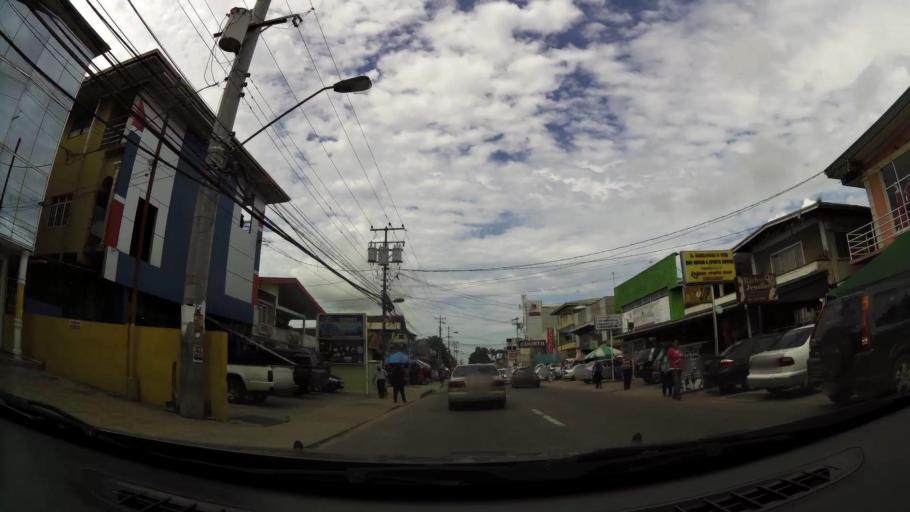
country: TT
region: Couva-Tabaquite-Talparo
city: Couva
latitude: 10.4218
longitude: -61.4577
